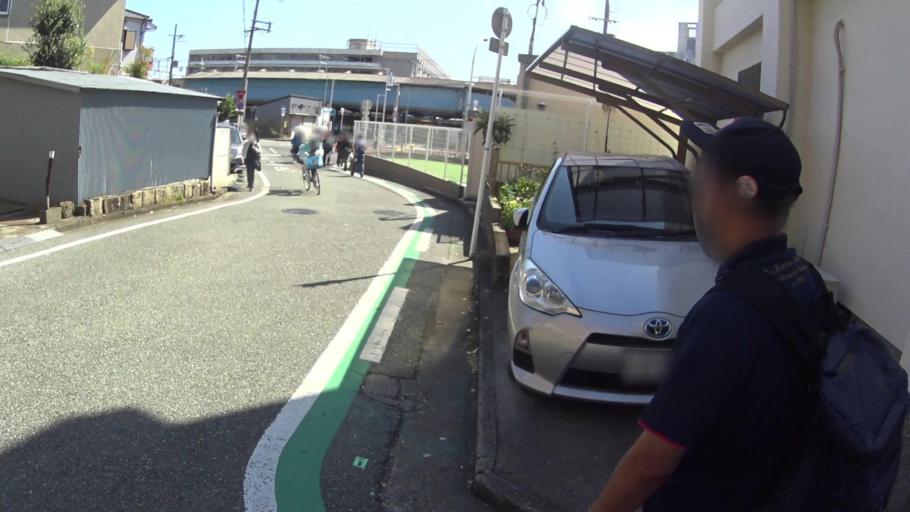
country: JP
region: Osaka
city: Izumiotsu
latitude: 34.4846
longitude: 135.3969
